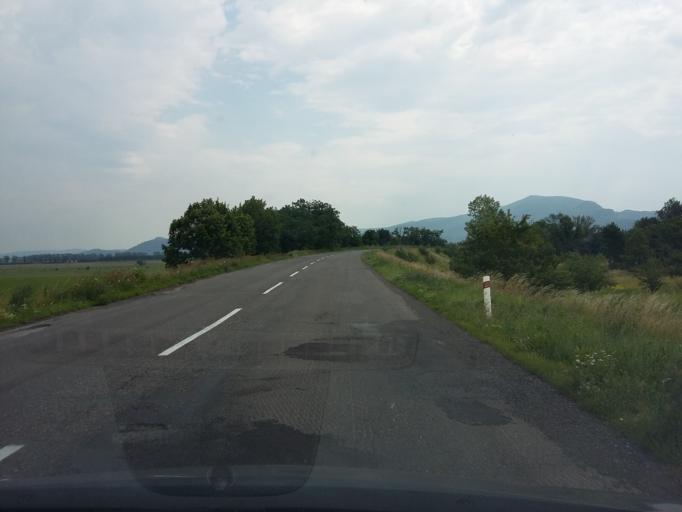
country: SK
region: Bratislavsky
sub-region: Okres Malacky
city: Malacky
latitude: 48.4616
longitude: 17.1887
